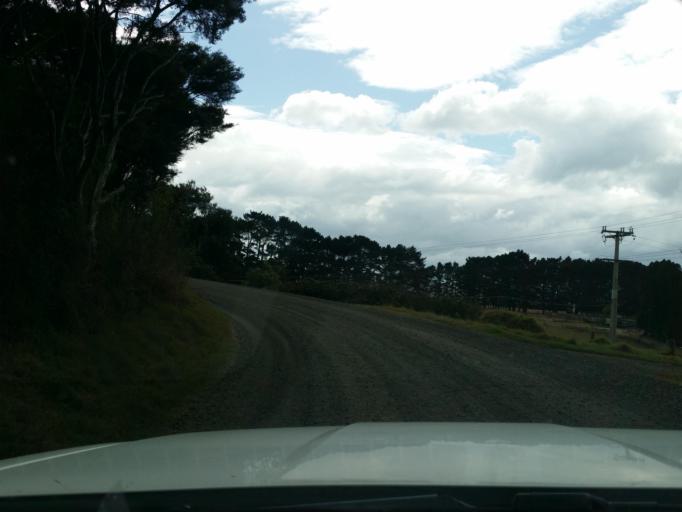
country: NZ
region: Auckland
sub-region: Auckland
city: Wellsford
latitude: -36.3158
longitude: 174.1345
